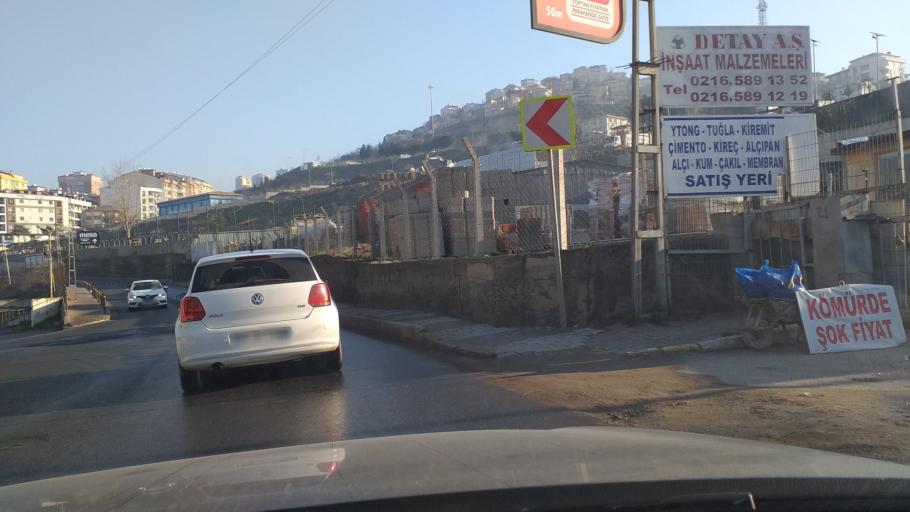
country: TR
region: Istanbul
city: Maltepe
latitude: 40.9326
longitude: 29.1523
